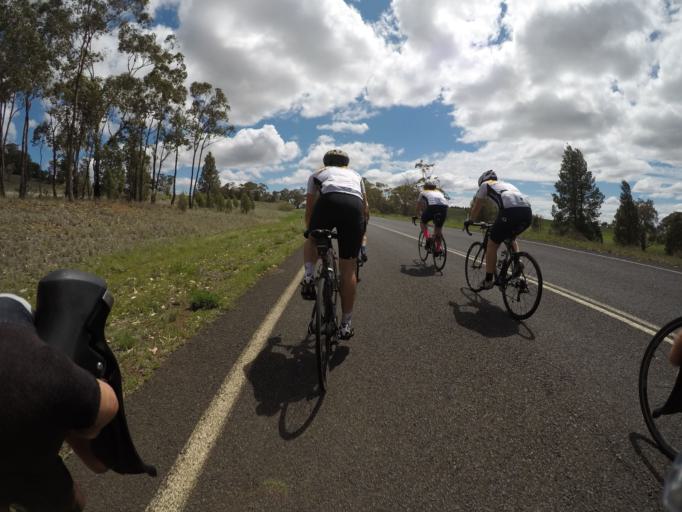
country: AU
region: New South Wales
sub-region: Dubbo Municipality
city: Dubbo
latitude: -32.4392
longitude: 148.5845
